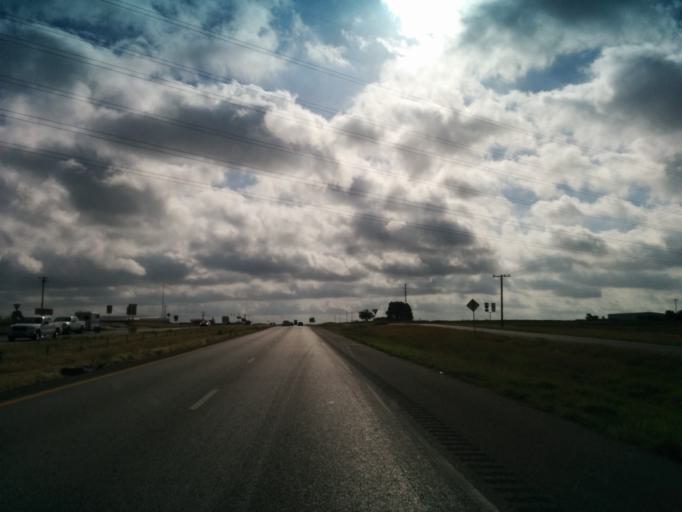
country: US
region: Texas
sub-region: Guadalupe County
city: Marion
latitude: 29.5363
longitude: -98.0847
